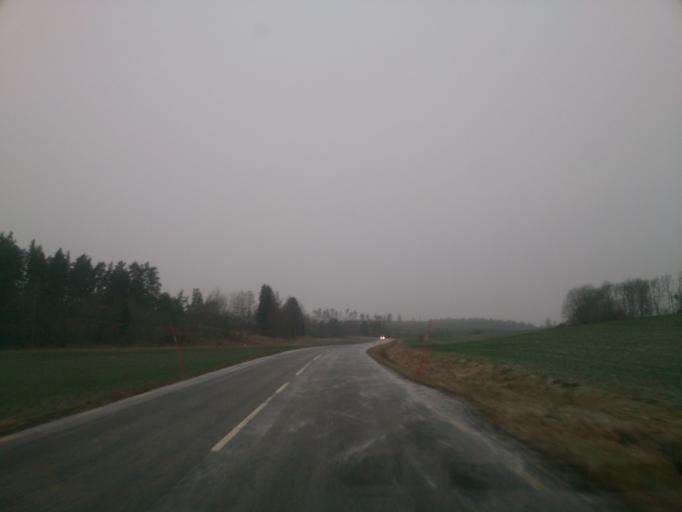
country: SE
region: OEstergoetland
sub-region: Soderkopings Kommun
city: Soederkoeping
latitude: 58.5146
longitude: 16.3427
